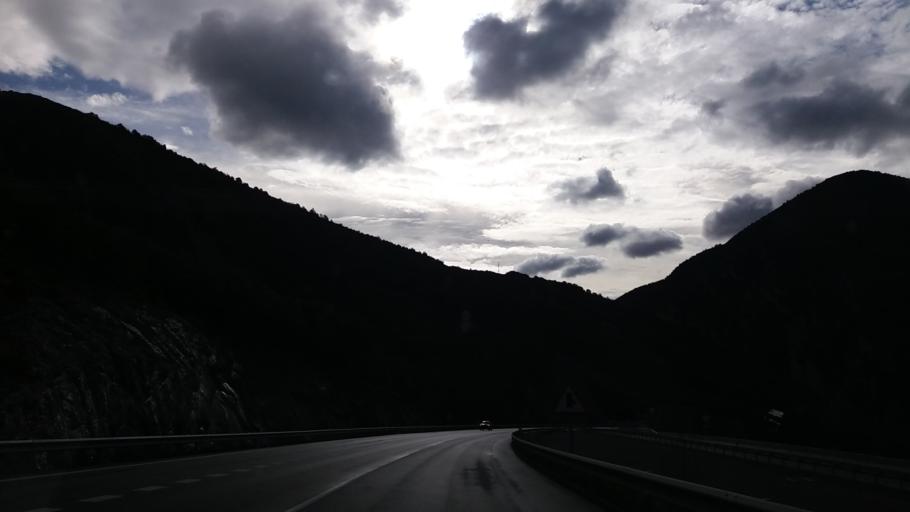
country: ES
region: Aragon
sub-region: Provincia de Huesca
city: Arguis
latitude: 42.3088
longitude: -0.4243
